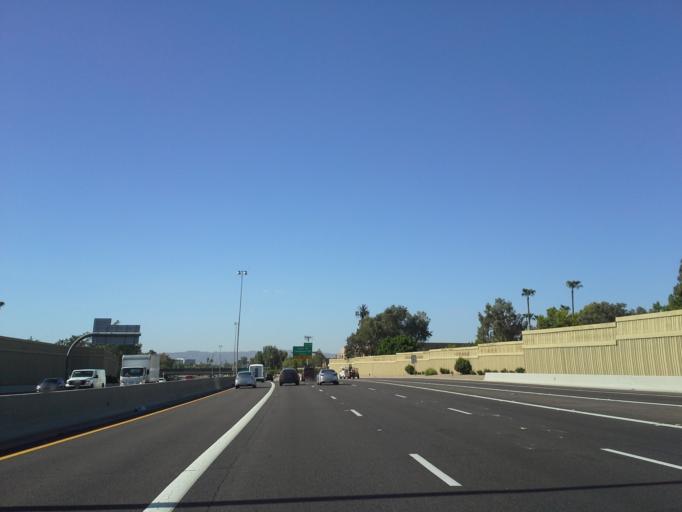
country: US
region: Arizona
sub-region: Maricopa County
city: Phoenix
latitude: 33.5206
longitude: -112.0442
